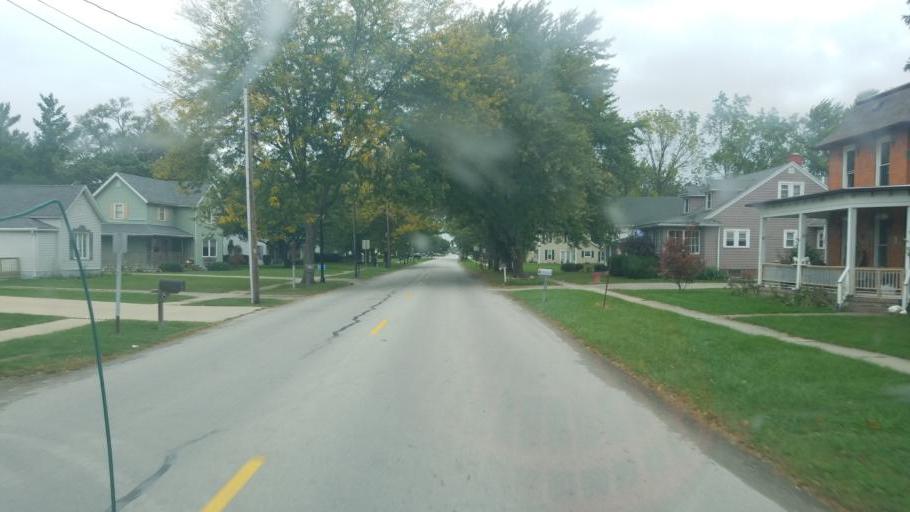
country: US
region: Ohio
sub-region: Wood County
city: Haskins
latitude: 41.4660
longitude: -83.7055
